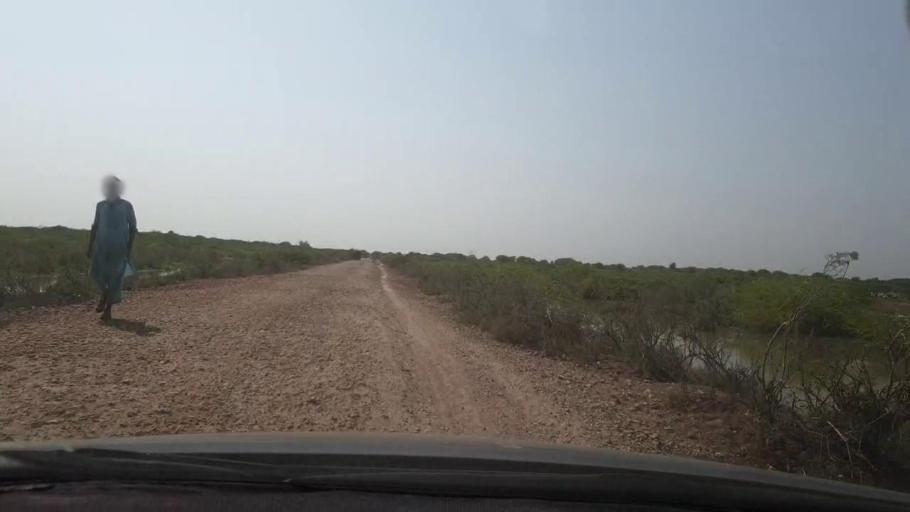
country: PK
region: Sindh
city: Naukot
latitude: 24.7959
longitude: 69.2302
